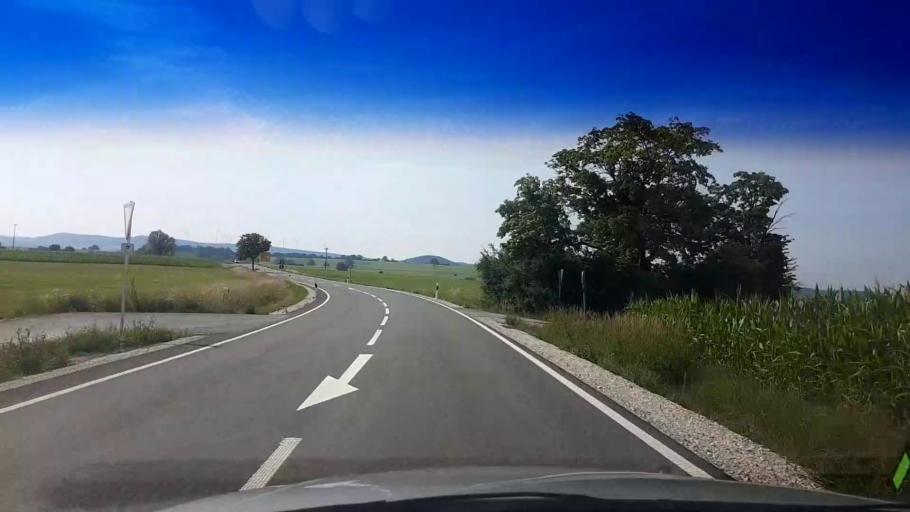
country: DE
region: Bavaria
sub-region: Upper Franconia
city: Mistelgau
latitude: 49.9341
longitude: 11.4723
